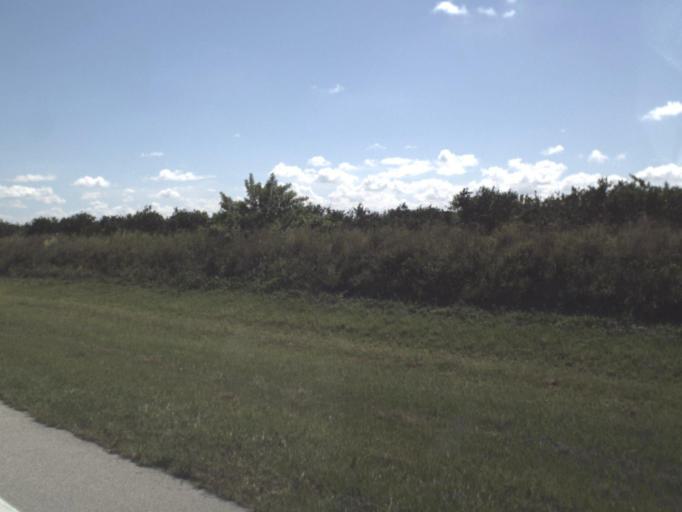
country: US
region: Florida
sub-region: Hendry County
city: Port LaBelle
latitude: 26.8128
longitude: -81.3498
